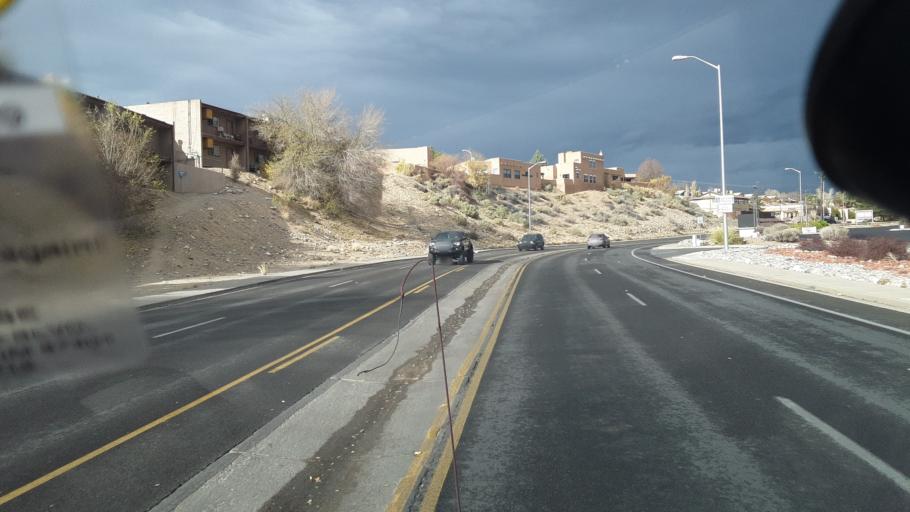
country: US
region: New Mexico
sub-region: San Juan County
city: Farmington
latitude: 36.7564
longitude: -108.1968
